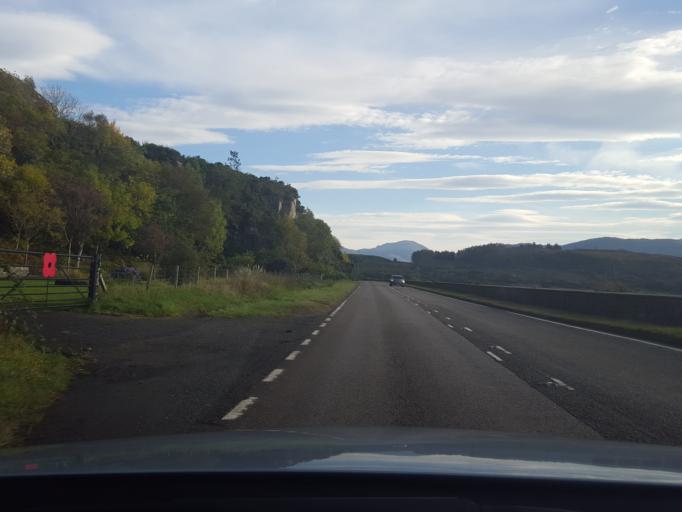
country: GB
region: Scotland
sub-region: Highland
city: Portree
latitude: 57.2831
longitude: -5.6370
